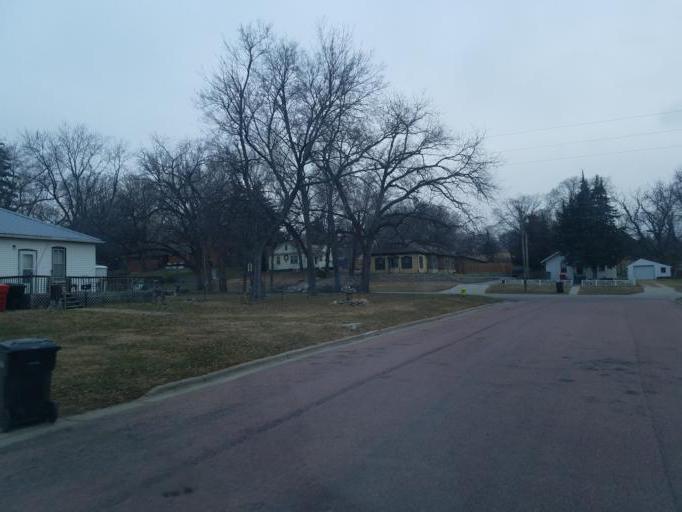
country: US
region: South Dakota
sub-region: Yankton County
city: Yankton
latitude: 42.8757
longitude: -97.4016
